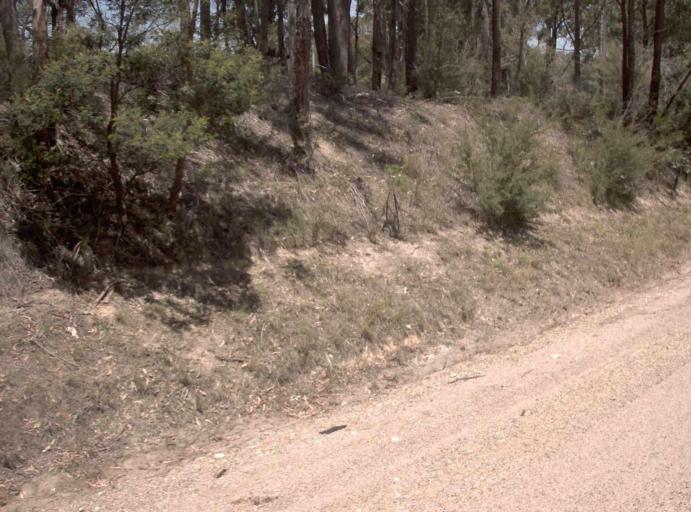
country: AU
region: Victoria
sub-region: East Gippsland
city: Bairnsdale
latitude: -37.7425
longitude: 147.7636
